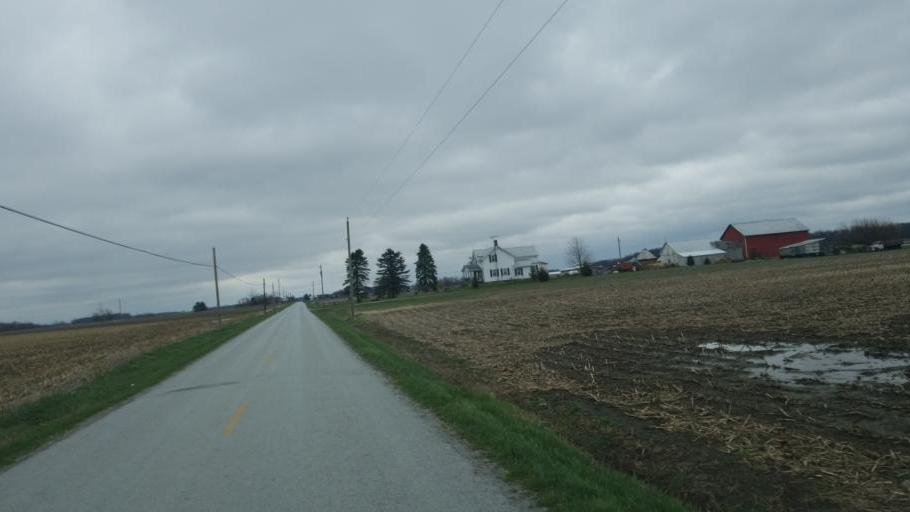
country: US
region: Ohio
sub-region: Hardin County
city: Kenton
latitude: 40.6577
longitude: -83.5043
